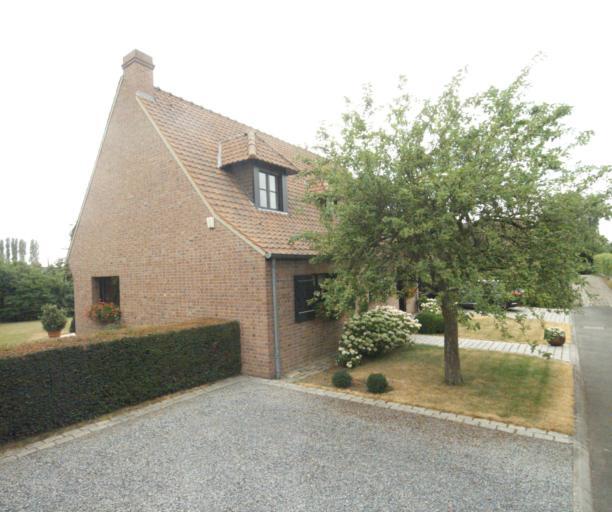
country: FR
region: Nord-Pas-de-Calais
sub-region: Departement du Nord
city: Neuville-en-Ferrain
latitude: 50.7472
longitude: 3.1512
